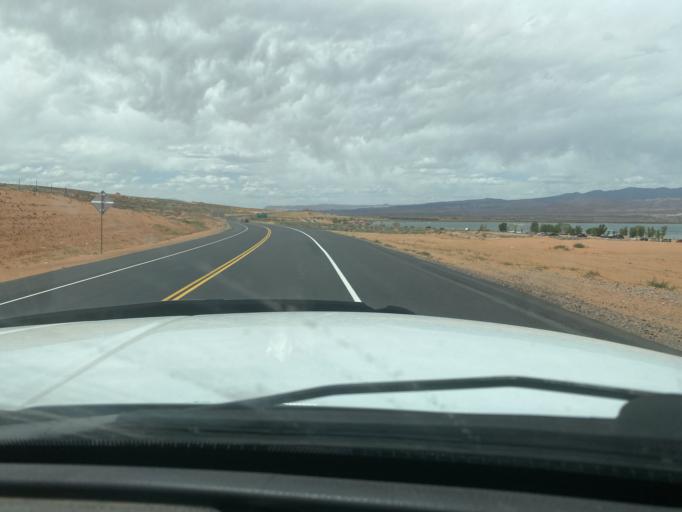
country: US
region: Utah
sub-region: Washington County
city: Hurricane
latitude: 37.1012
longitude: -113.3814
